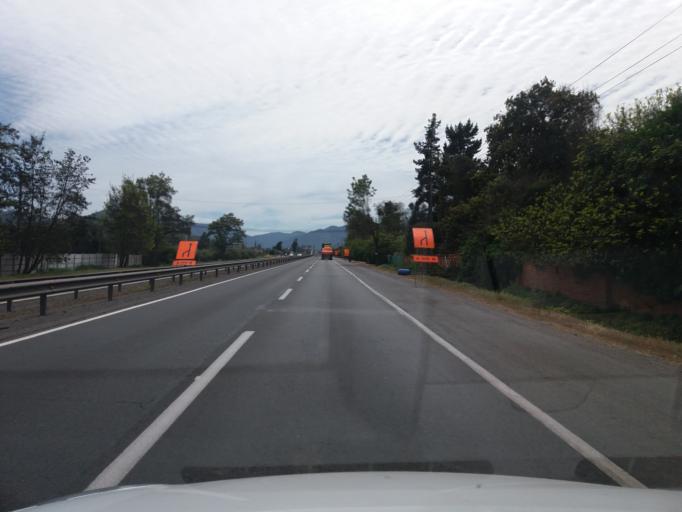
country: CL
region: Valparaiso
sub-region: Provincia de Quillota
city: Hacienda La Calera
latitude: -32.7184
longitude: -71.2044
